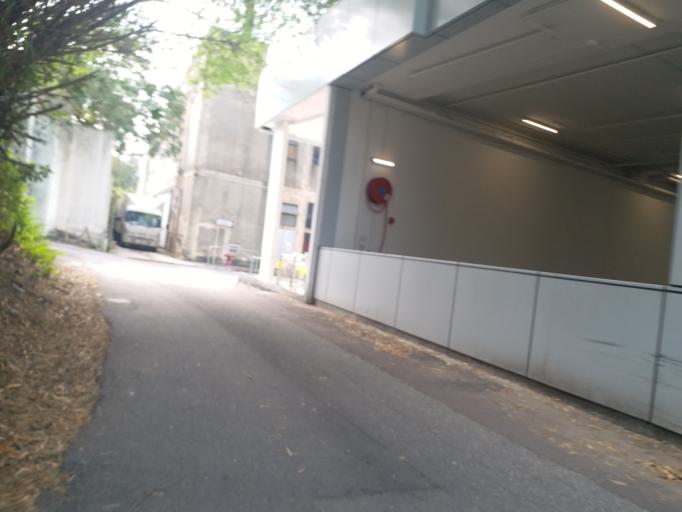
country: HK
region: Yuen Long
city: Yuen Long Kau Hui
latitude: 22.4429
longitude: 114.0035
